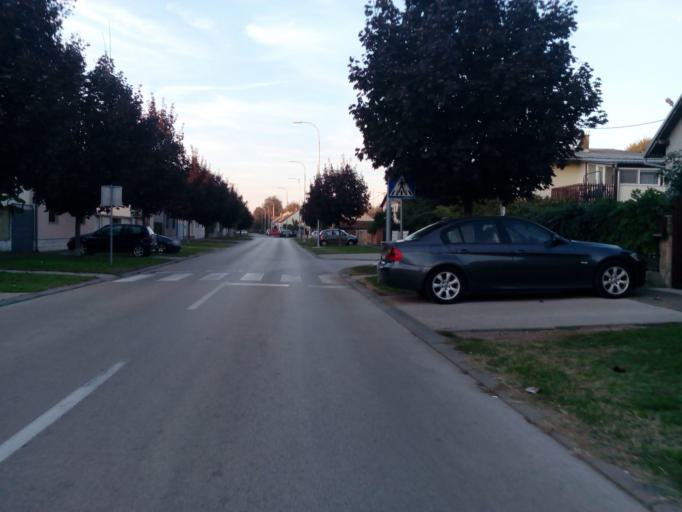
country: HR
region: Vukovarsko-Srijemska
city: Vinkovci
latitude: 45.2968
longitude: 18.8164
